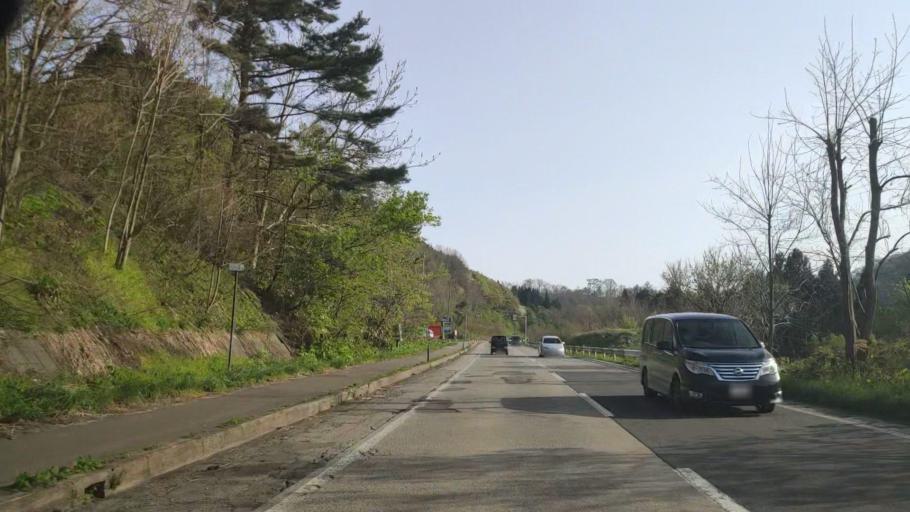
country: JP
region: Aomori
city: Aomori Shi
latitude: 40.8652
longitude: 140.8457
